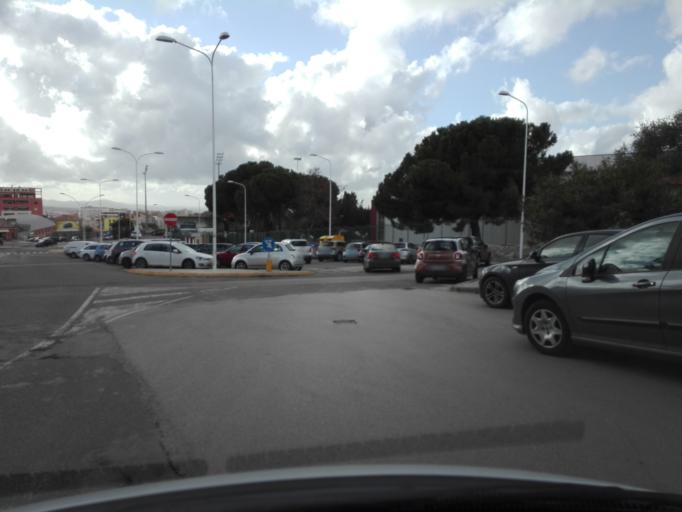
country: IT
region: Sardinia
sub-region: Provincia di Sassari
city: Sassari
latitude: 40.7161
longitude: 8.5835
